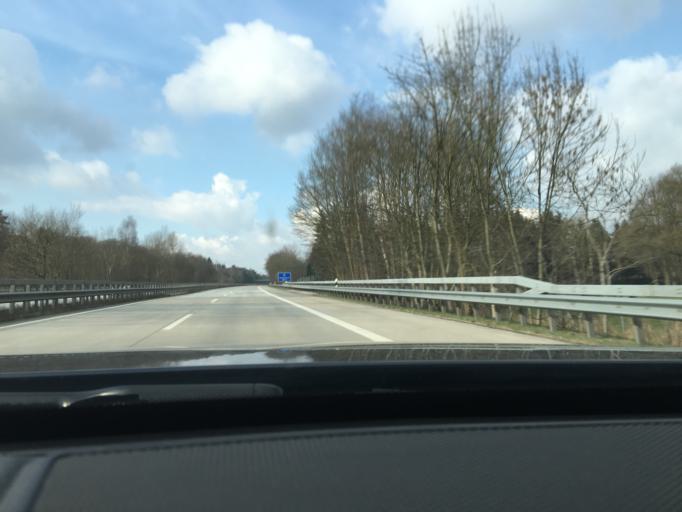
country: DE
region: Lower Saxony
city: Lemwerder
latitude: 53.2045
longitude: 8.6701
